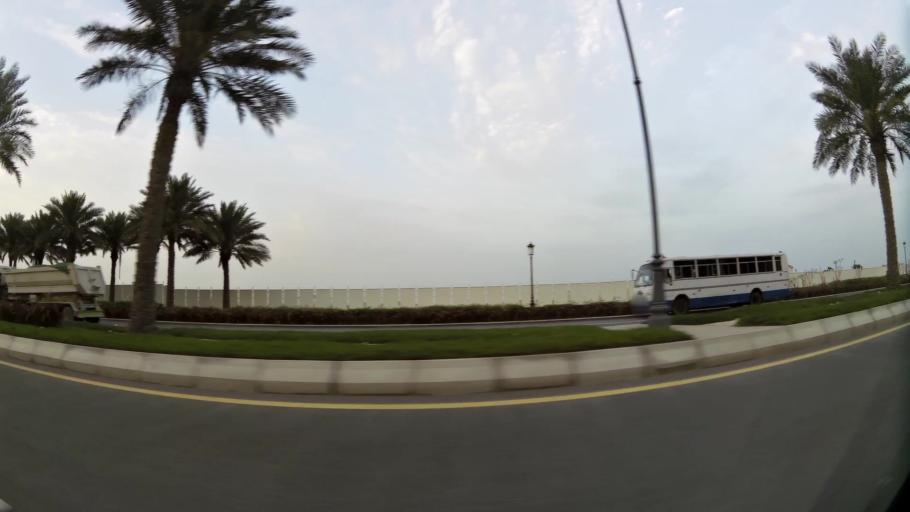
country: QA
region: Baladiyat ad Dawhah
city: Doha
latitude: 25.3706
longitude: 51.5608
